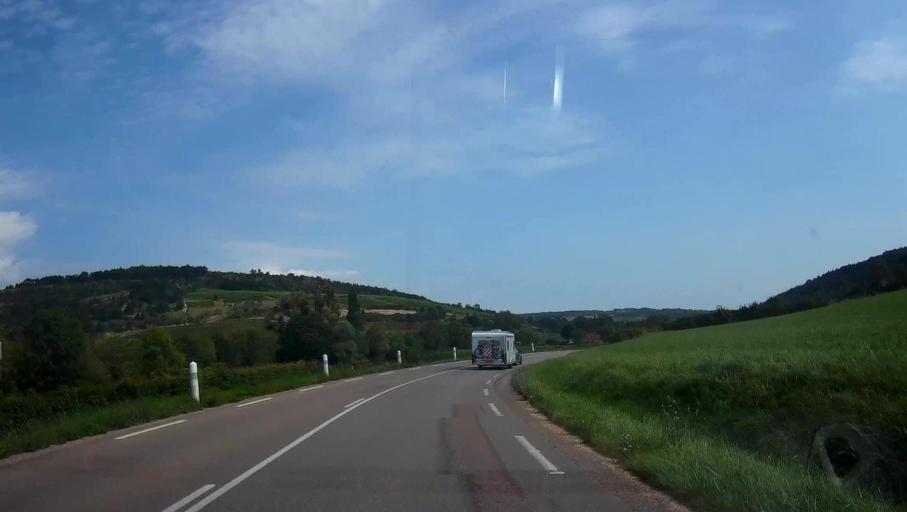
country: FR
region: Bourgogne
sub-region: Departement de la Cote-d'Or
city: Meursault
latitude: 46.9770
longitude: 4.7035
